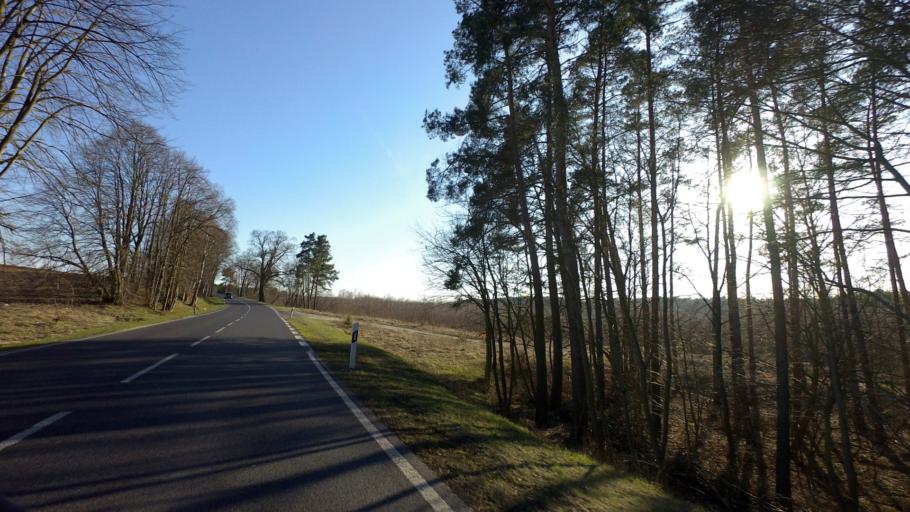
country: DE
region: Brandenburg
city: Althuttendorf
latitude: 52.9324
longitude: 13.7917
